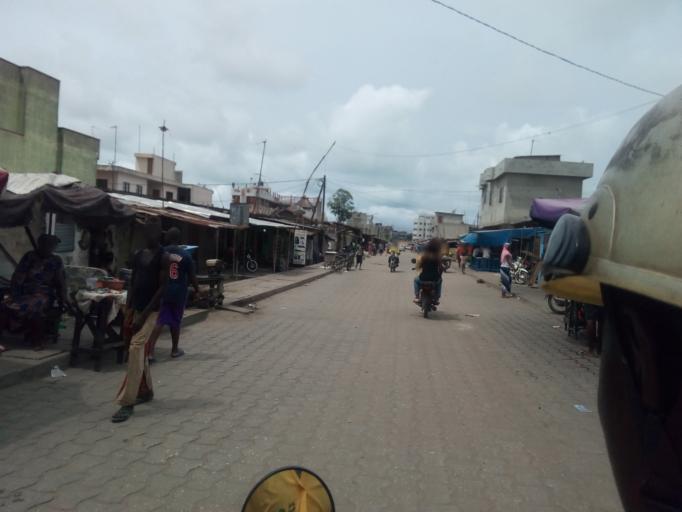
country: BJ
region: Littoral
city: Cotonou
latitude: 6.3752
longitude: 2.4392
